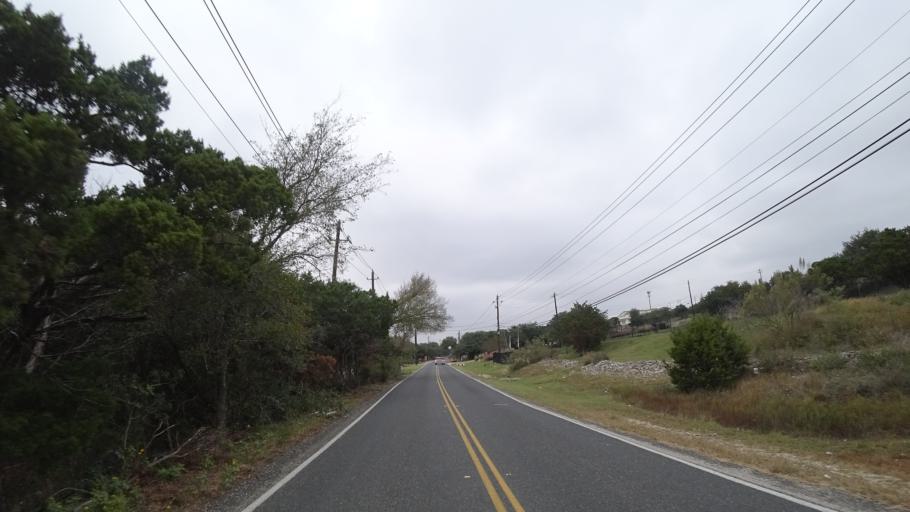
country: US
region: Texas
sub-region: Travis County
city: Barton Creek
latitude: 30.2399
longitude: -97.8764
